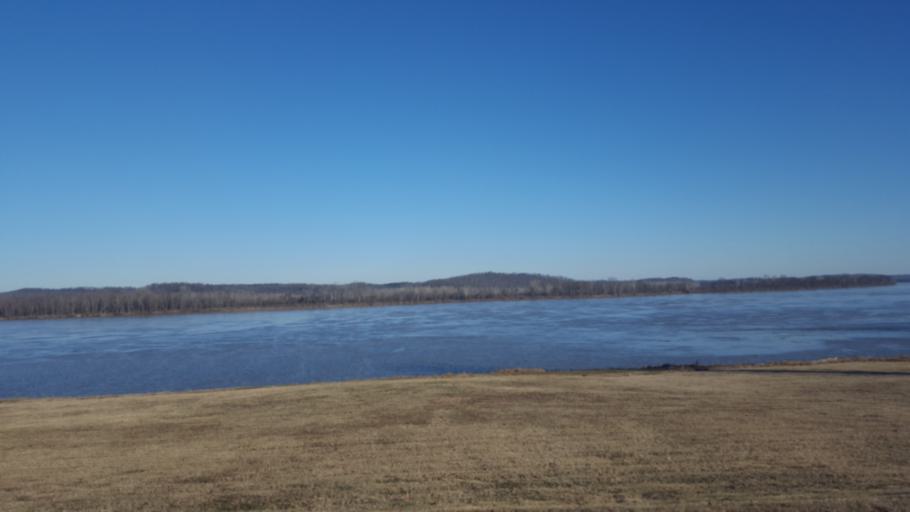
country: US
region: Kentucky
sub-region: Crittenden County
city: Marion
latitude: 37.4662
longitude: -88.0931
